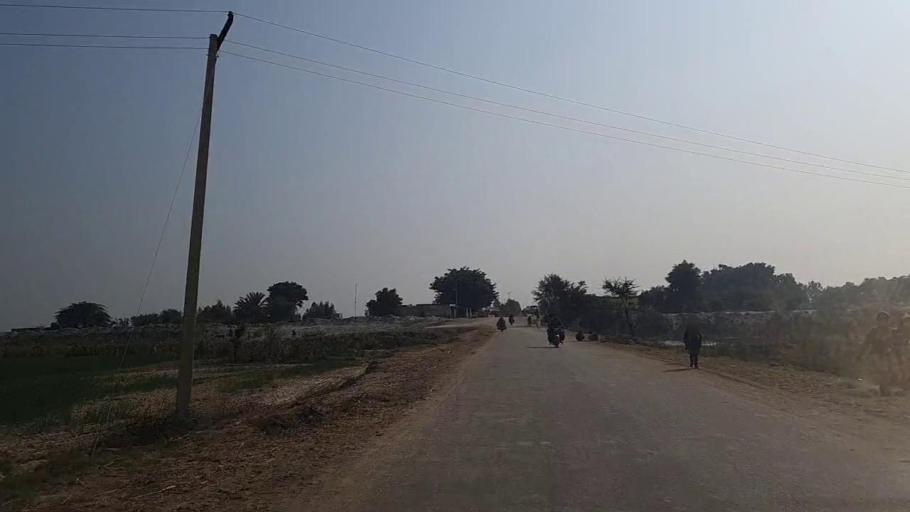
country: PK
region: Sindh
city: Jam Sahib
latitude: 26.3338
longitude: 68.5366
